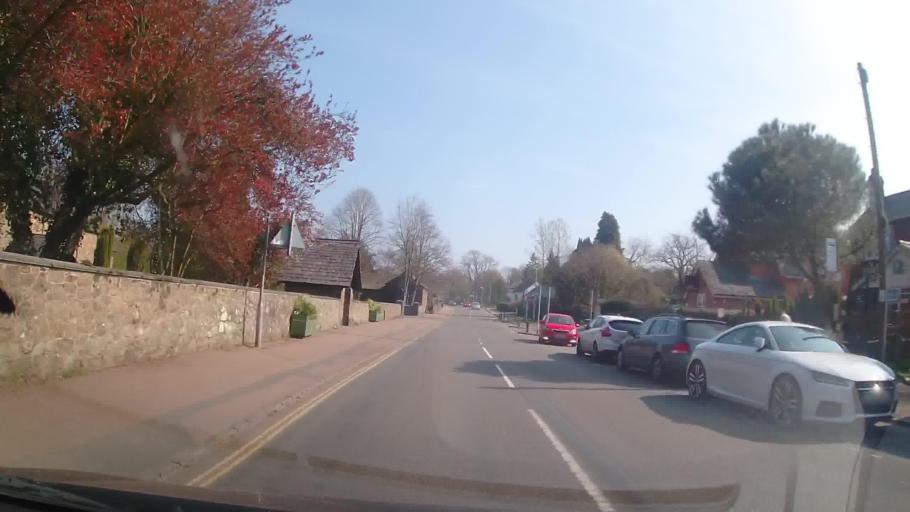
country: GB
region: England
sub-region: Leicestershire
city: Anstey
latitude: 52.6831
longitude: -1.2296
